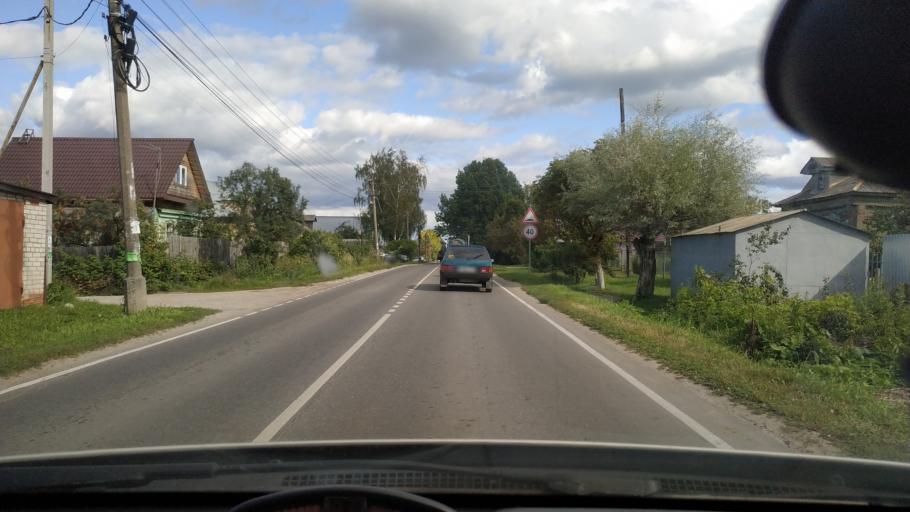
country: RU
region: Moskovskaya
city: Fryazevo
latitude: 55.7235
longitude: 38.4589
